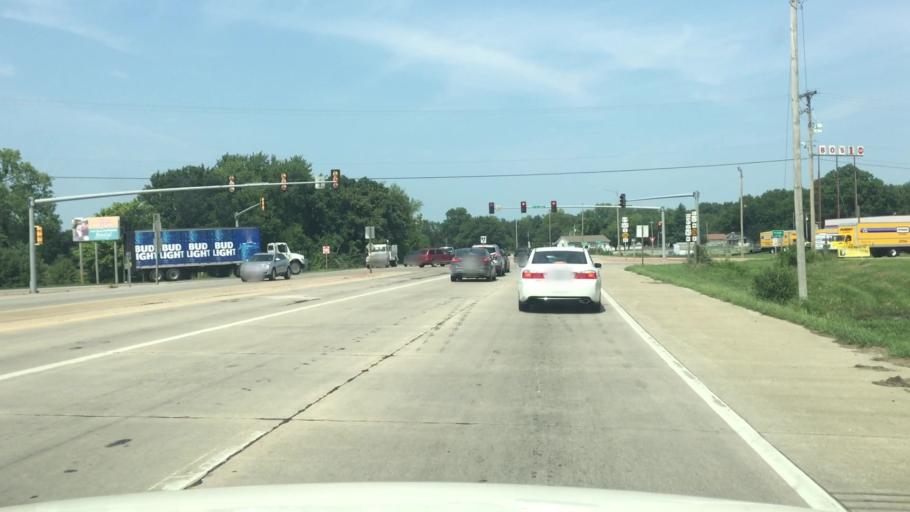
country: US
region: Kansas
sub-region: Crawford County
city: Pittsburg
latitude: 37.4106
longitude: -94.7241
